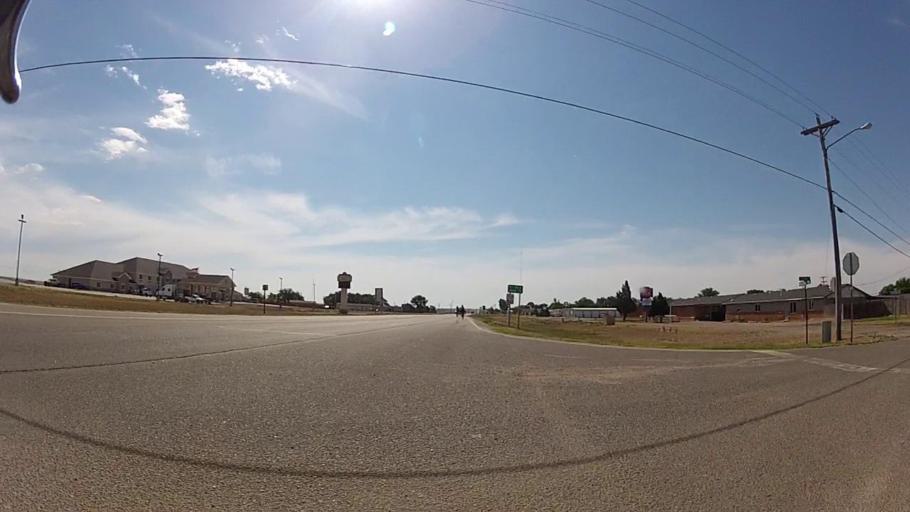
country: US
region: Kansas
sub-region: Grant County
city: Ulysses
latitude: 37.5750
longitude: -101.3454
